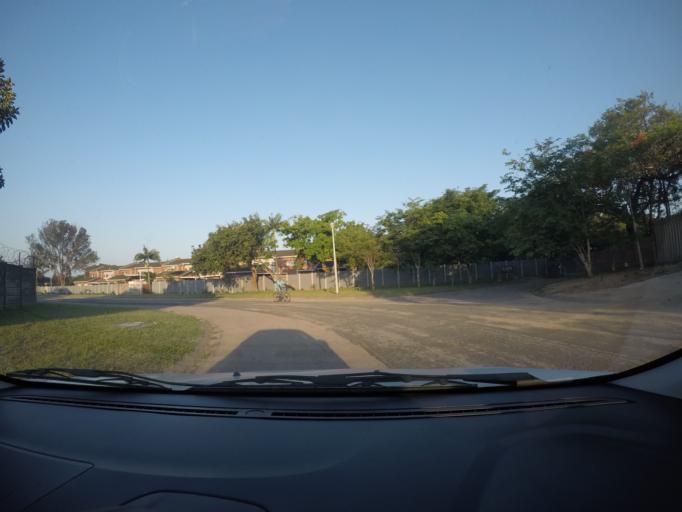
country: ZA
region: KwaZulu-Natal
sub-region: uThungulu District Municipality
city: Richards Bay
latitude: -28.7812
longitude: 32.1016
